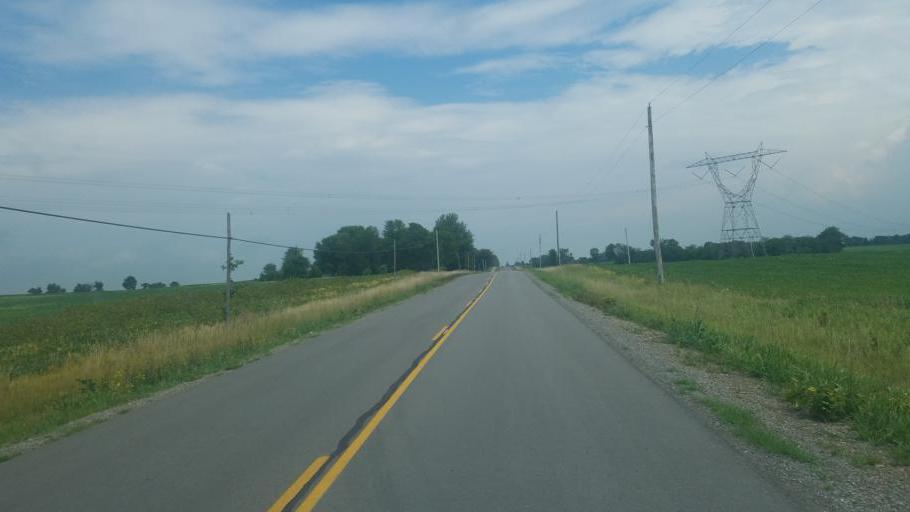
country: US
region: Ohio
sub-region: Logan County
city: Northwood
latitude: 40.3920
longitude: -83.5842
